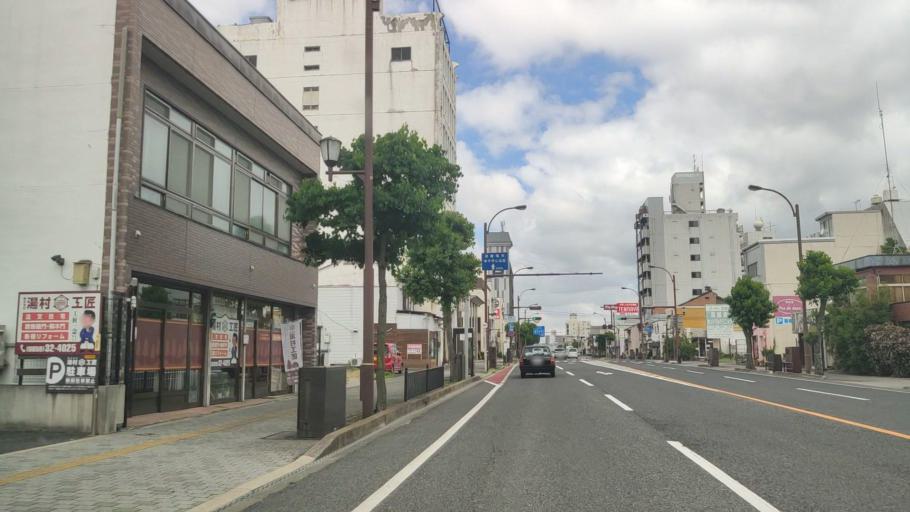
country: JP
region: Tottori
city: Yonago
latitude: 35.4318
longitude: 133.3356
